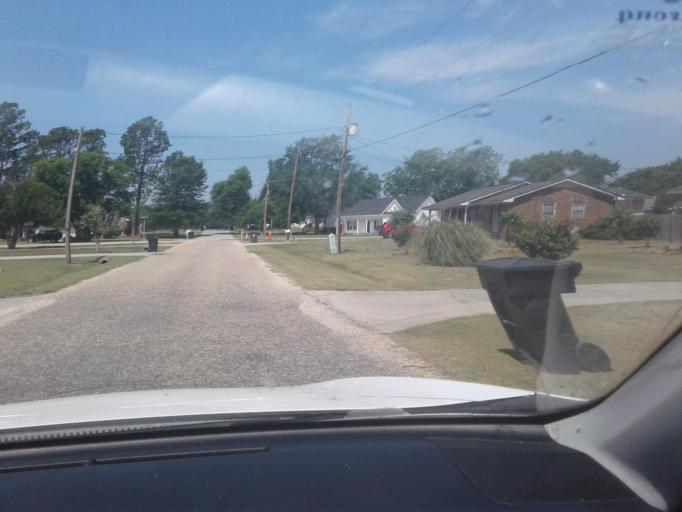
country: US
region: North Carolina
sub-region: Harnett County
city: Erwin
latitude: 35.3227
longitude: -78.6815
